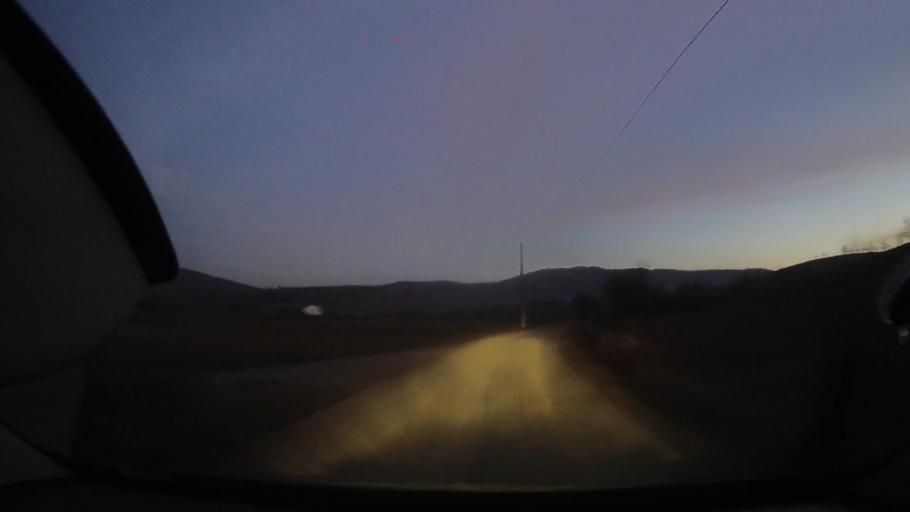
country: RO
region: Bihor
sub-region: Comuna Varciorog
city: Varciorog
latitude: 46.9883
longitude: 22.3271
